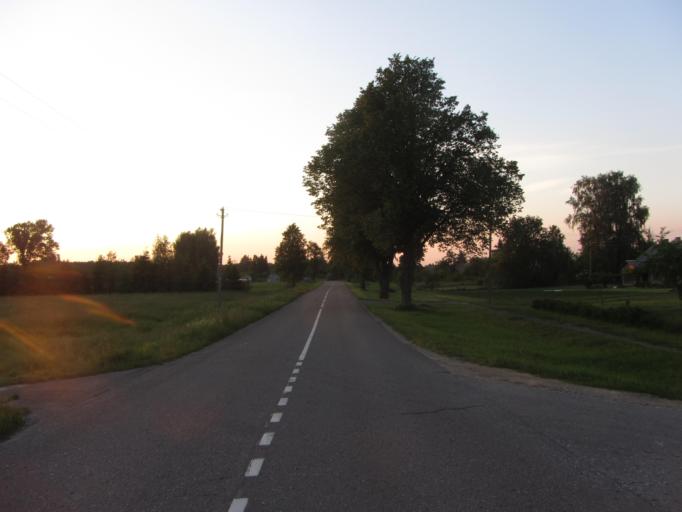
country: LT
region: Alytaus apskritis
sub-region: Alytaus rajonas
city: Daugai
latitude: 54.4266
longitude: 24.3409
